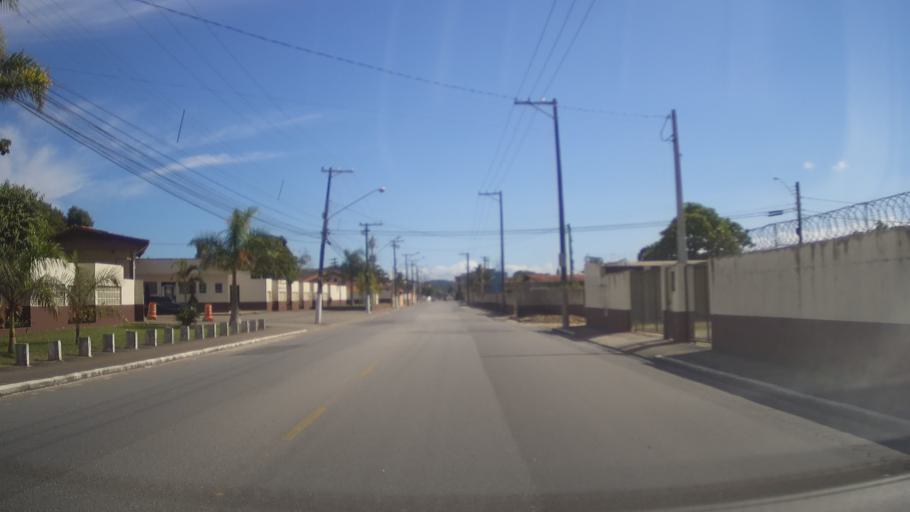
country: BR
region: Sao Paulo
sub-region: Itanhaem
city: Itanhaem
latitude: -24.1745
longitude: -46.7706
